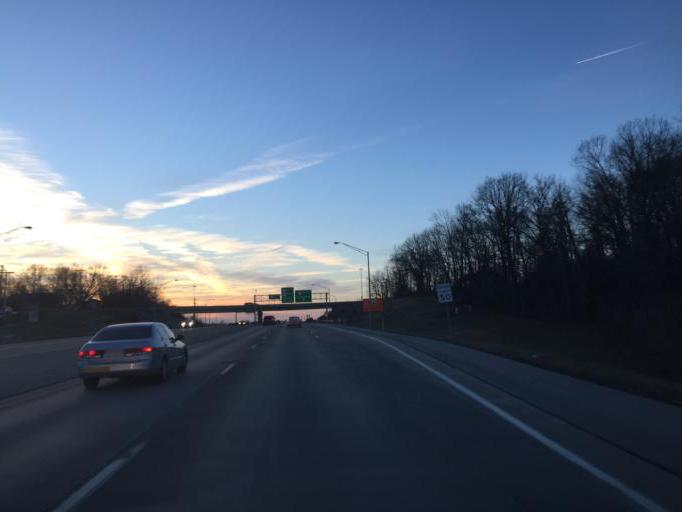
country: US
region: Indiana
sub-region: Monroe County
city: Bloomington
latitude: 39.1870
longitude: -86.5490
